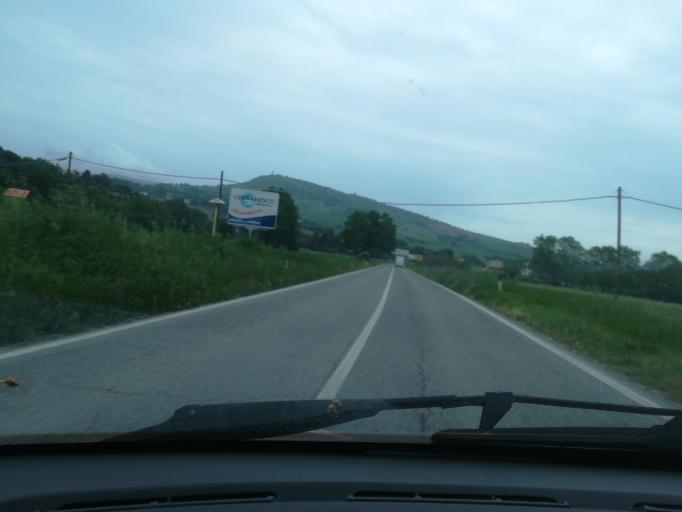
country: IT
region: The Marches
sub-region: Provincia di Macerata
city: San Severino Marche
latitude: 43.2524
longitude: 13.2310
